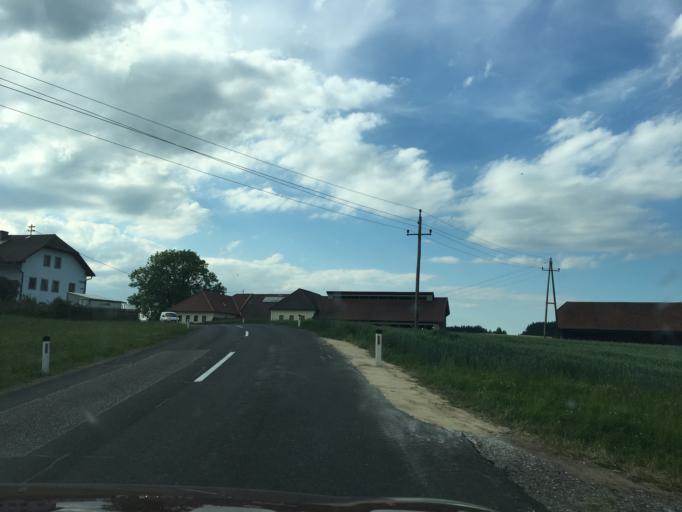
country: AT
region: Upper Austria
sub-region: Politischer Bezirk Urfahr-Umgebung
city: Reichenau im Muhlkreis
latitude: 48.4729
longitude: 14.3418
